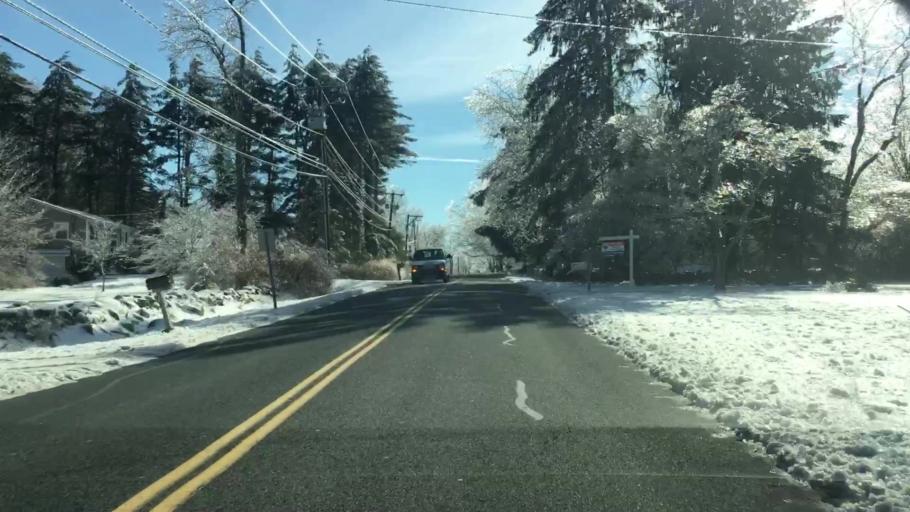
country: US
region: Connecticut
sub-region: Fairfield County
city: Trumbull
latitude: 41.3254
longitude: -73.2212
